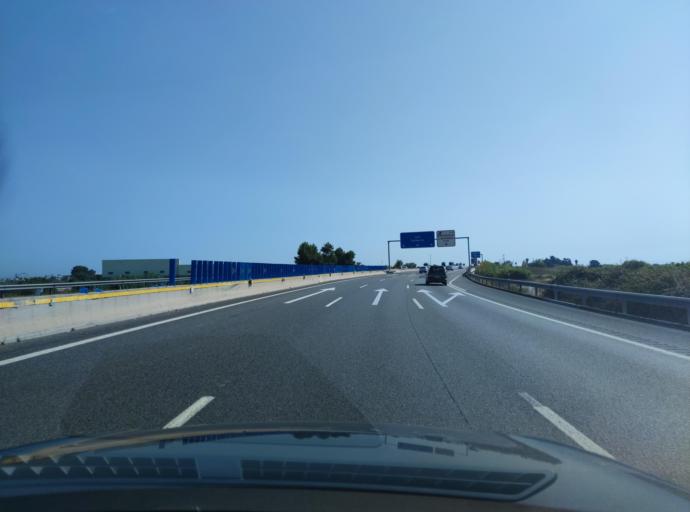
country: ES
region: Valencia
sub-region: Provincia de Valencia
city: L'Alcudia
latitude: 39.1824
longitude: -0.5124
